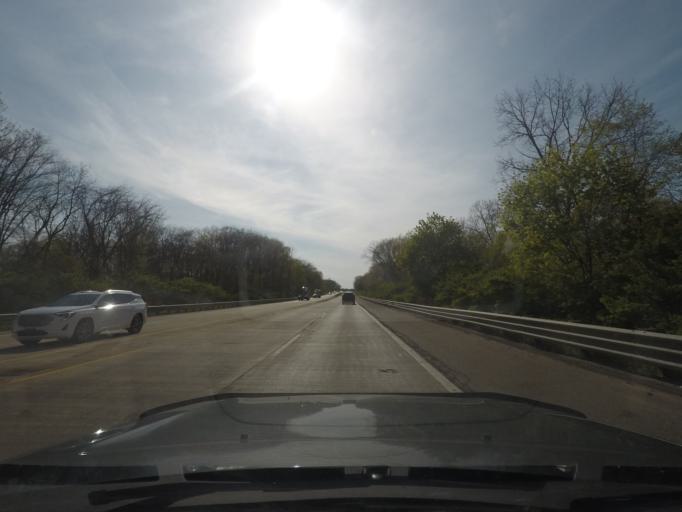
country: US
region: Michigan
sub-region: Berrien County
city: Niles
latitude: 41.8013
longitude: -86.2686
